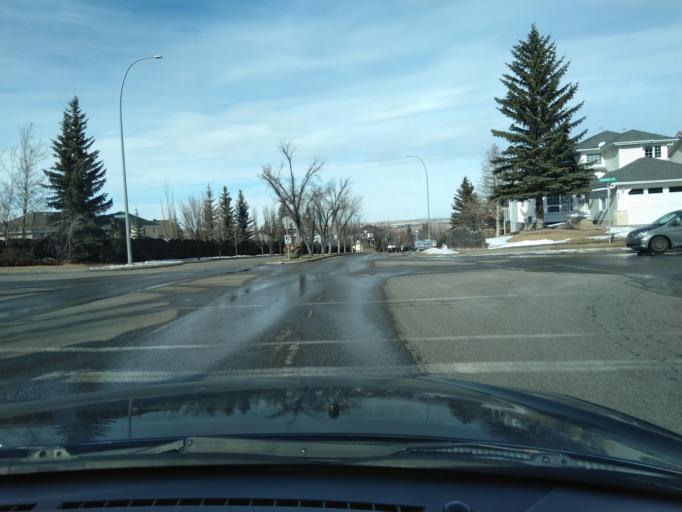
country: CA
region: Alberta
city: Calgary
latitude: 51.1345
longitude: -114.1342
